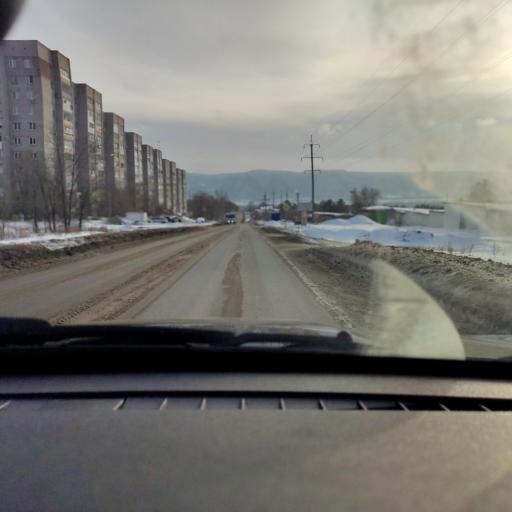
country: RU
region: Samara
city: Pribrezhnyy
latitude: 53.4926
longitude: 49.8475
